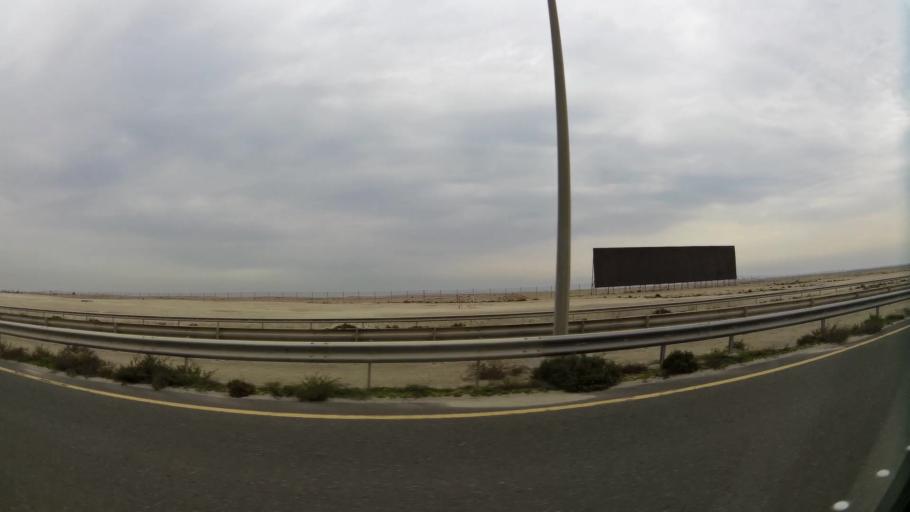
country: BH
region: Central Governorate
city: Dar Kulayb
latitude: 25.8739
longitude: 50.5792
